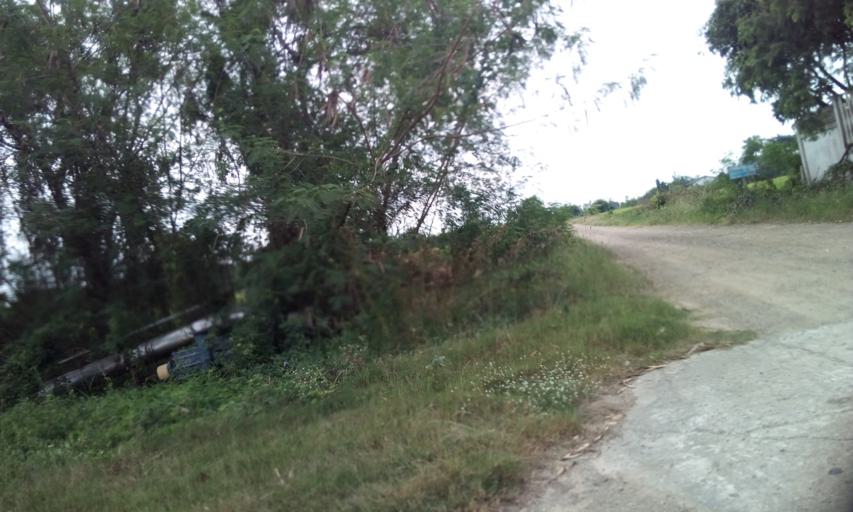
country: TH
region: Pathum Thani
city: Nong Suea
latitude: 14.0644
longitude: 100.8704
